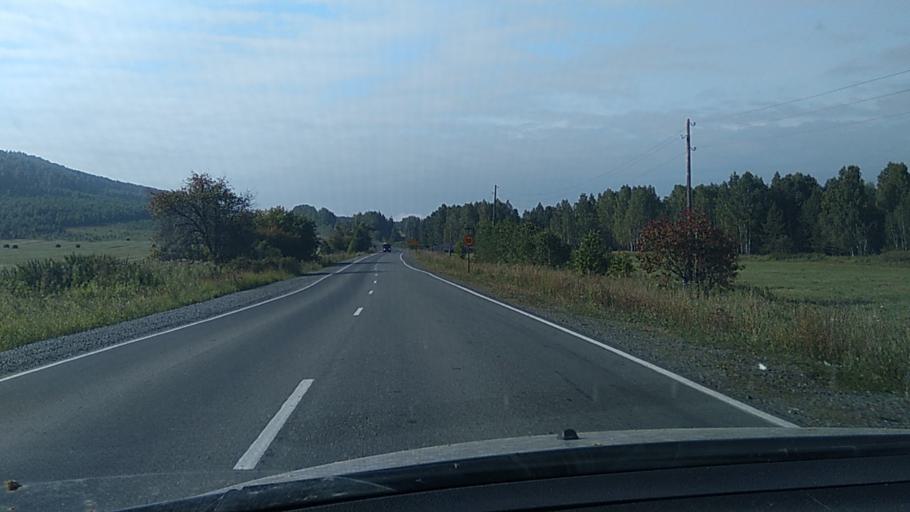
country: RU
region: Chelyabinsk
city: Karabash
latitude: 55.3805
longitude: 60.2544
